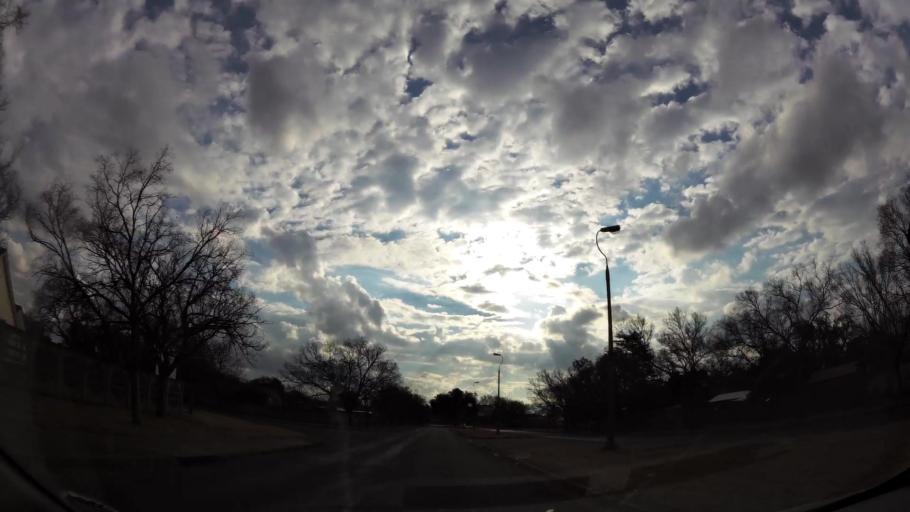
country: ZA
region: Orange Free State
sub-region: Fezile Dabi District Municipality
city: Sasolburg
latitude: -26.8189
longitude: 27.8218
